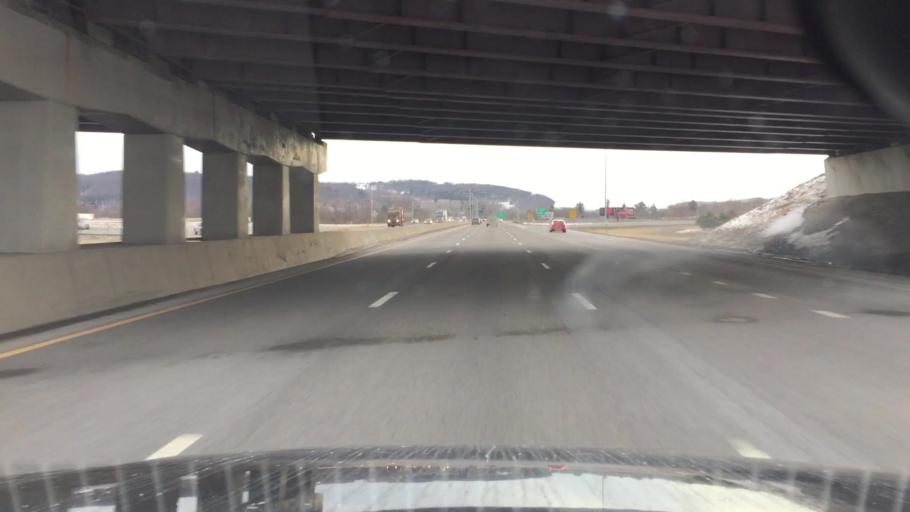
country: US
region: New York
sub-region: Broome County
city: Johnson City
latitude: 42.1200
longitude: -75.9694
